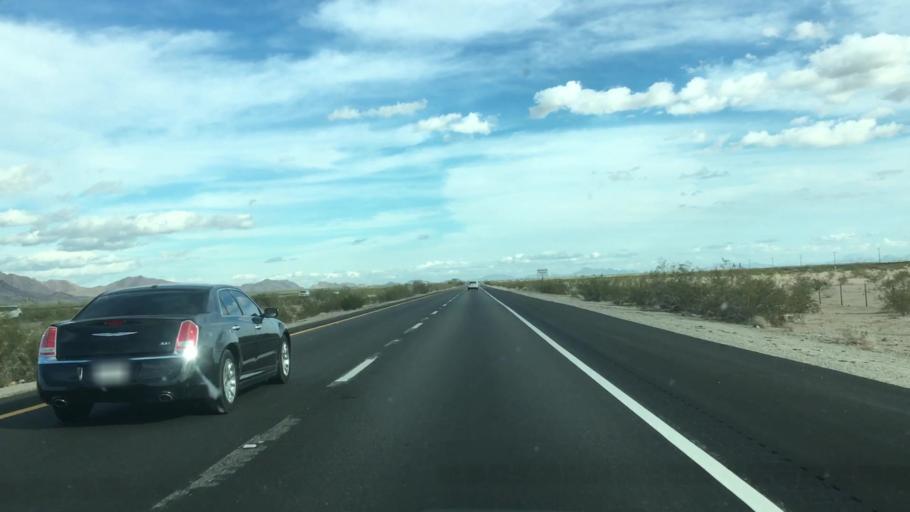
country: US
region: California
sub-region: Riverside County
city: Mesa Verde
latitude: 33.6079
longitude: -114.8918
